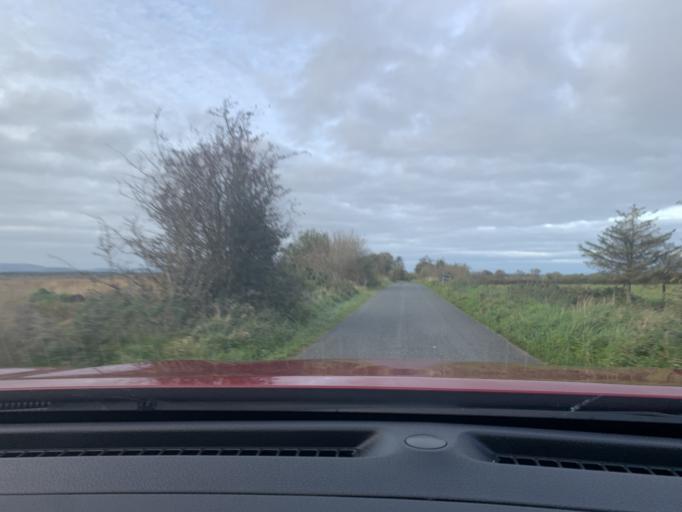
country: IE
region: Connaught
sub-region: Roscommon
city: Ballaghaderreen
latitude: 53.9883
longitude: -8.6130
